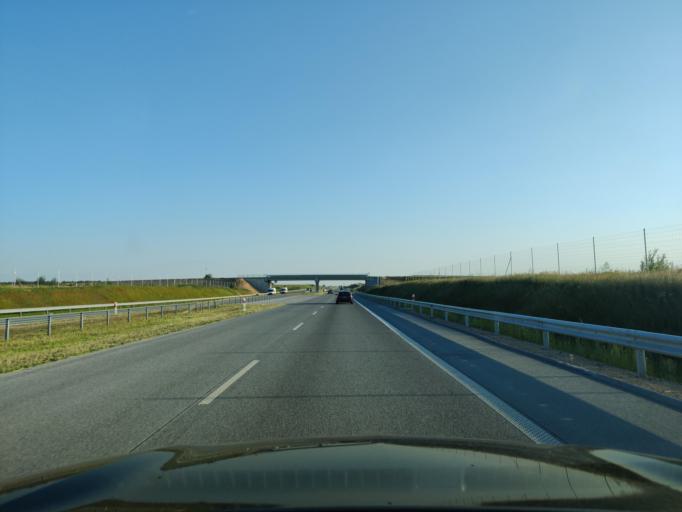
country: PL
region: Masovian Voivodeship
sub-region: Powiat mlawski
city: Wisniewo
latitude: 53.0288
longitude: 20.3484
